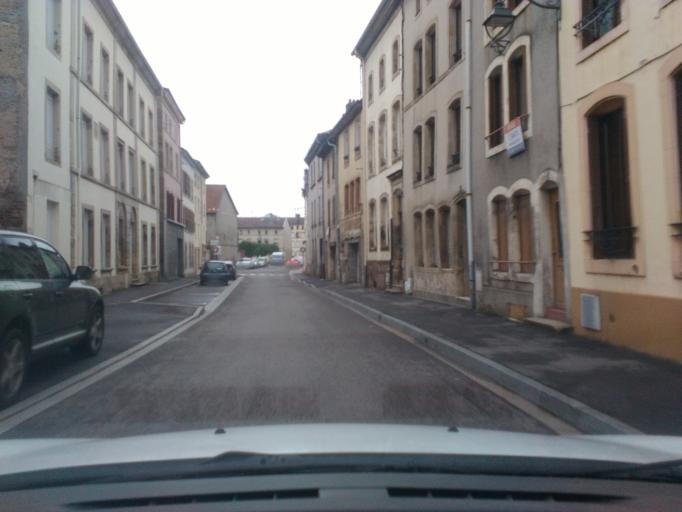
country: FR
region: Lorraine
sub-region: Departement des Vosges
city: Rambervillers
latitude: 48.3467
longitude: 6.6366
